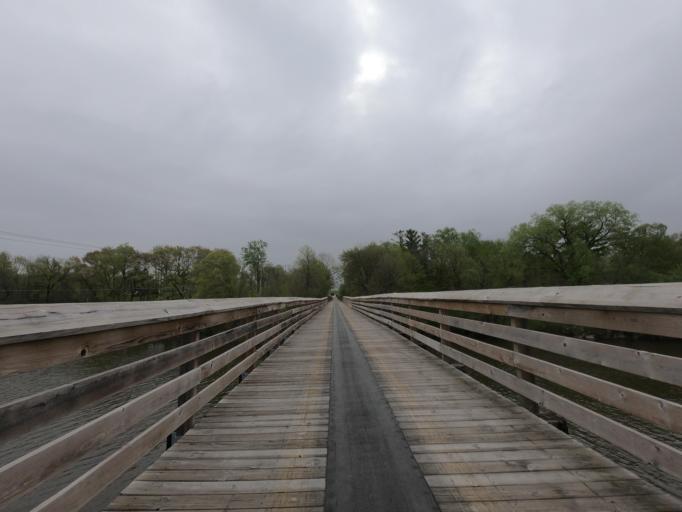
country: US
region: Wisconsin
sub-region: Jefferson County
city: Jefferson
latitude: 43.0366
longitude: -88.8105
